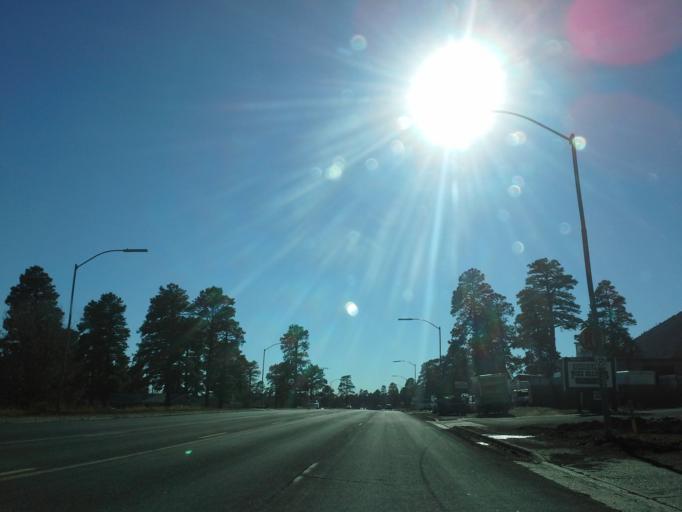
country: US
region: Arizona
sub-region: Coconino County
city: Flagstaff
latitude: 35.2414
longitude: -111.5692
